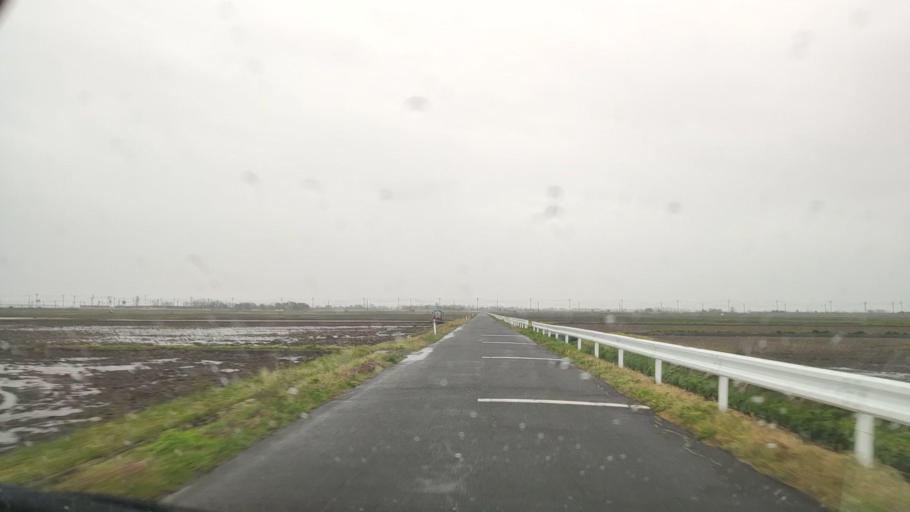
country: JP
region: Akita
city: Noshiromachi
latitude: 40.1022
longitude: 139.9977
